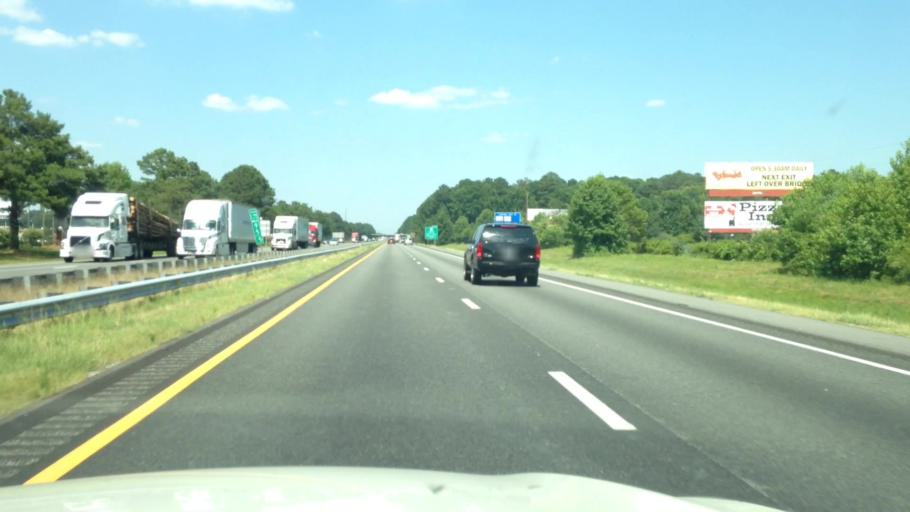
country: US
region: North Carolina
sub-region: Johnston County
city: Smithfield
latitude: 35.5093
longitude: -78.3101
